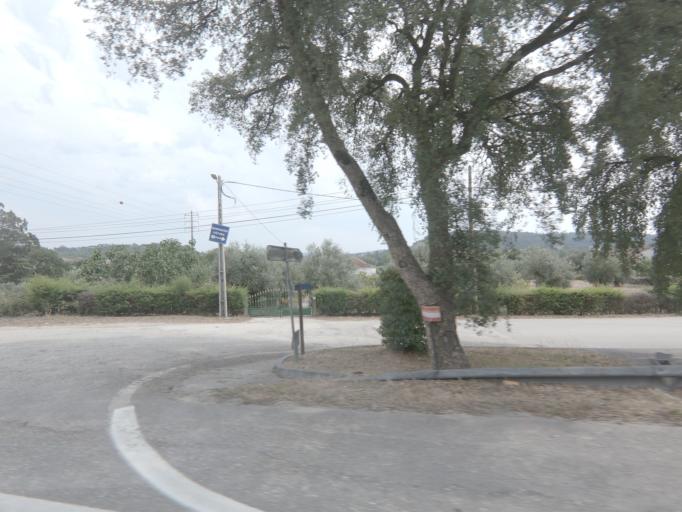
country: PT
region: Leiria
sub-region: Pombal
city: Pombal
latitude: 39.9001
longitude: -8.6401
